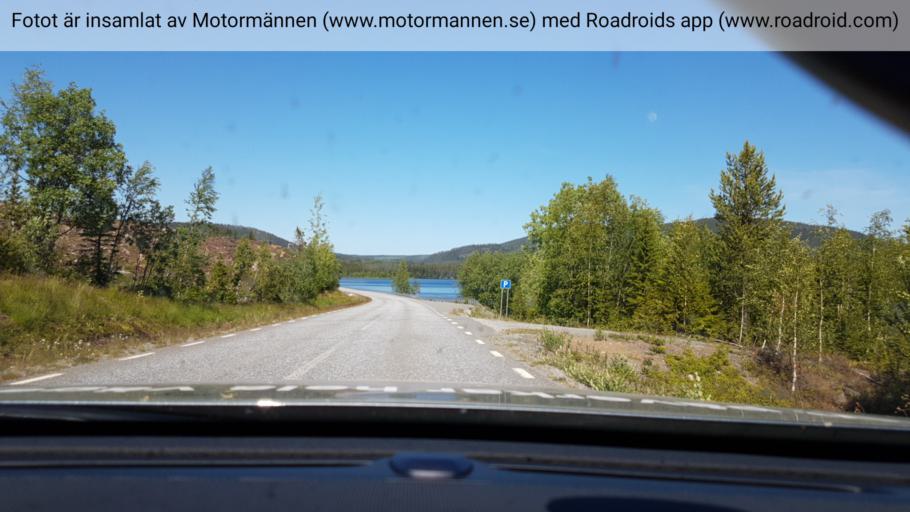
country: SE
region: Vaesterbotten
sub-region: Vilhelmina Kommun
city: Sjoberg
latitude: 64.9207
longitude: 15.8690
